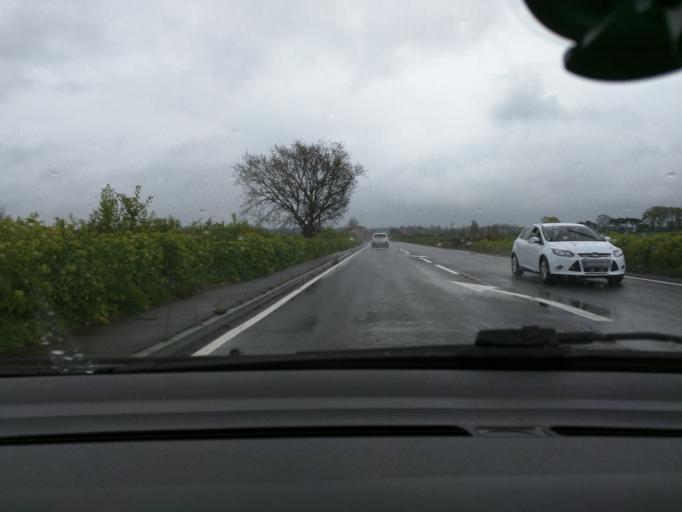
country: GB
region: England
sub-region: Suffolk
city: Wickham Market
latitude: 52.1658
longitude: 1.3918
